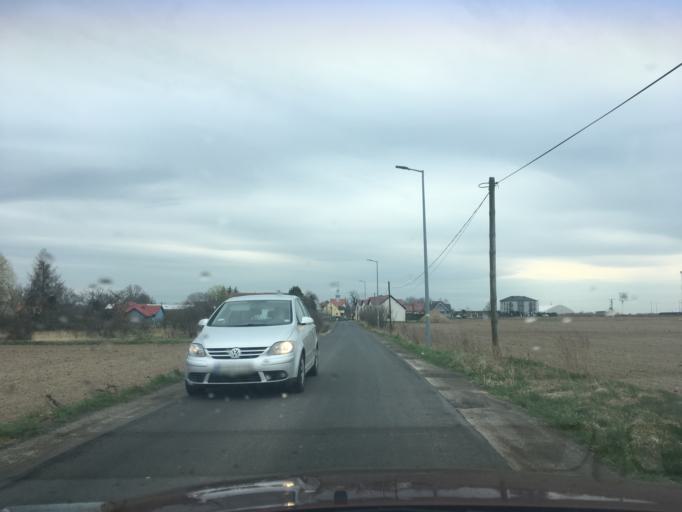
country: PL
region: Lower Silesian Voivodeship
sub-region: Powiat zgorzelecki
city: Lagow
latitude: 51.1625
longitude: 15.0402
